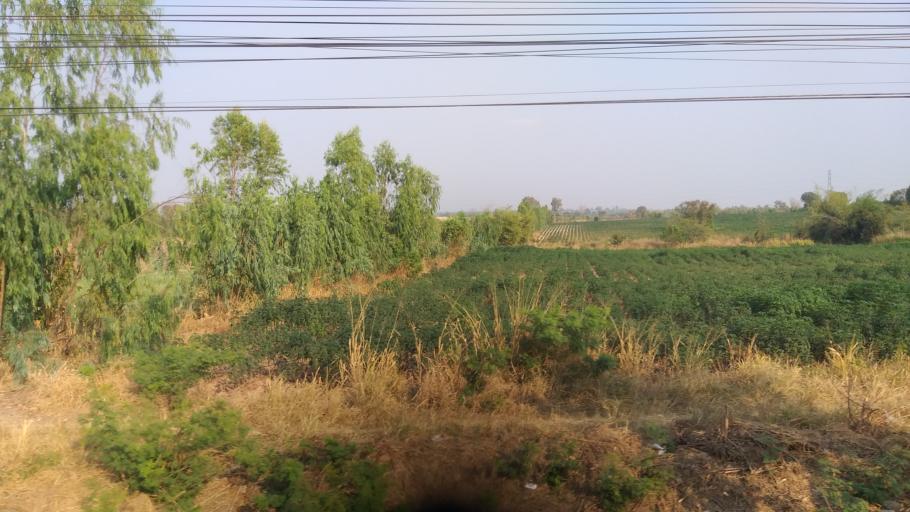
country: TH
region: Khon Kaen
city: Nam Phong
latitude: 16.6921
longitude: 102.8048
